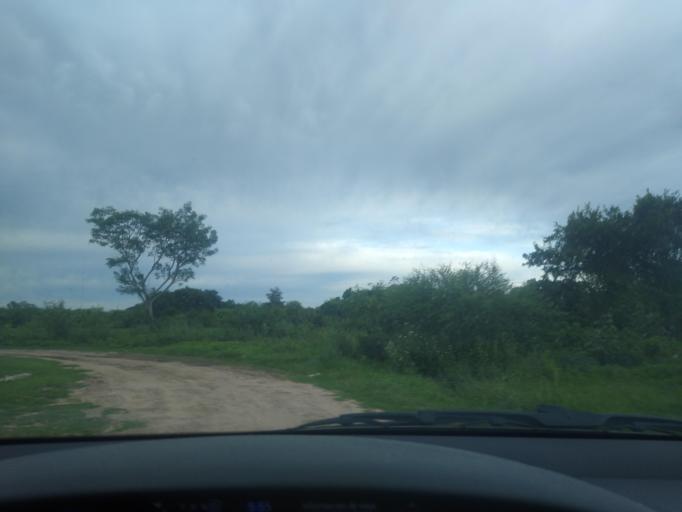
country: AR
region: Chaco
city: Barranqueras
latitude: -27.4654
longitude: -58.9453
